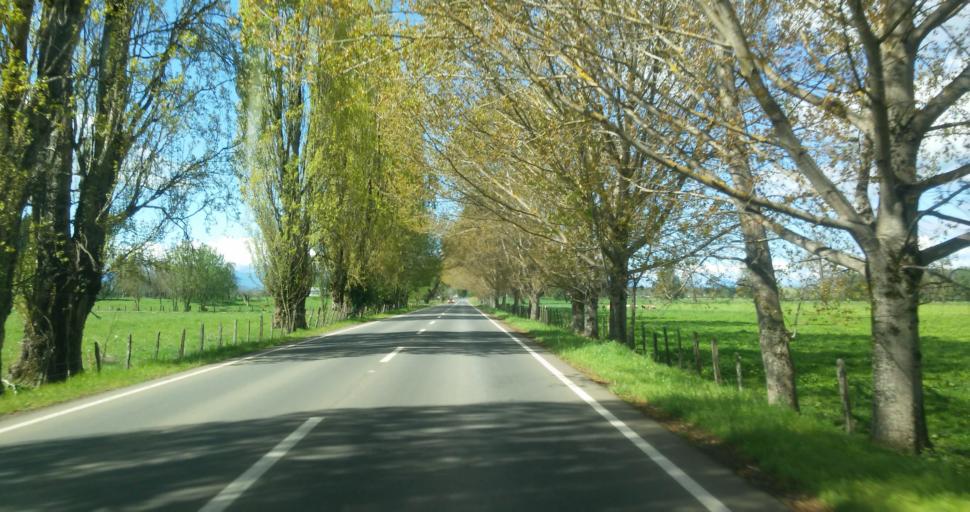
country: CL
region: Los Rios
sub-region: Provincia del Ranco
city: Rio Bueno
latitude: -40.2425
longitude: -72.6113
